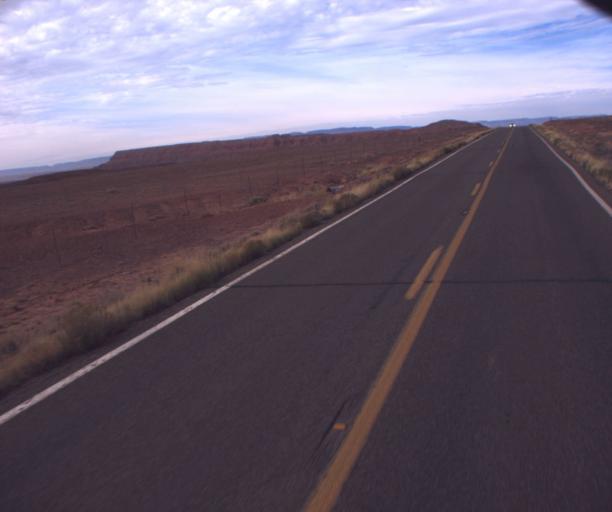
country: US
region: Arizona
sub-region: Apache County
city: Many Farms
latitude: 36.4693
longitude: -109.5327
